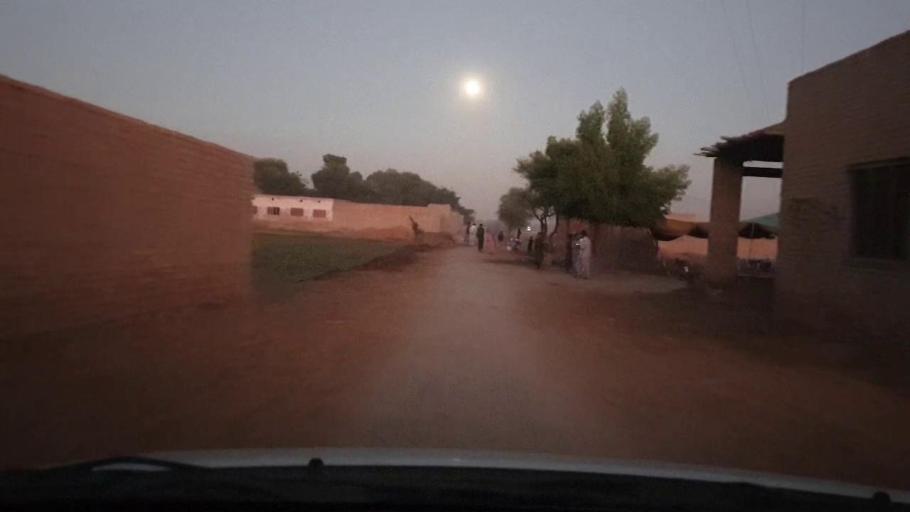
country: PK
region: Sindh
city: Khairpur Nathan Shah
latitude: 27.1332
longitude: 67.7297
